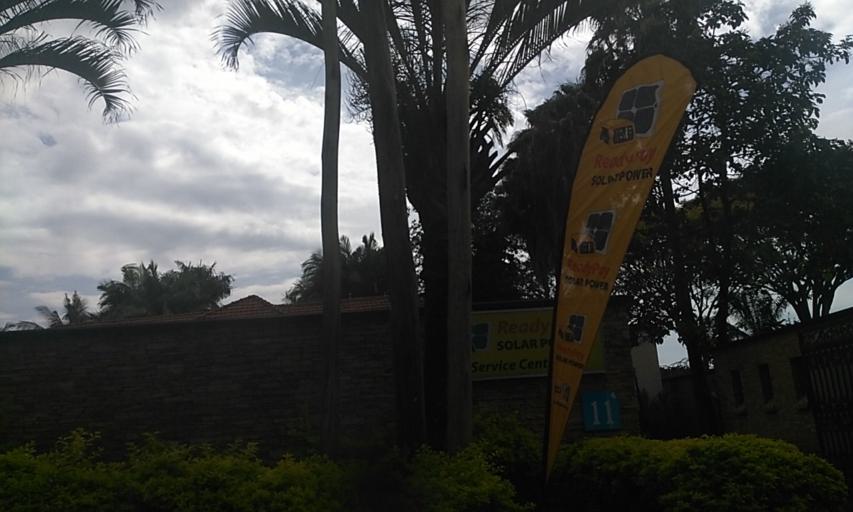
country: UG
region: Central Region
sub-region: Kampala District
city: Kampala
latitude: 0.3225
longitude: 32.5961
